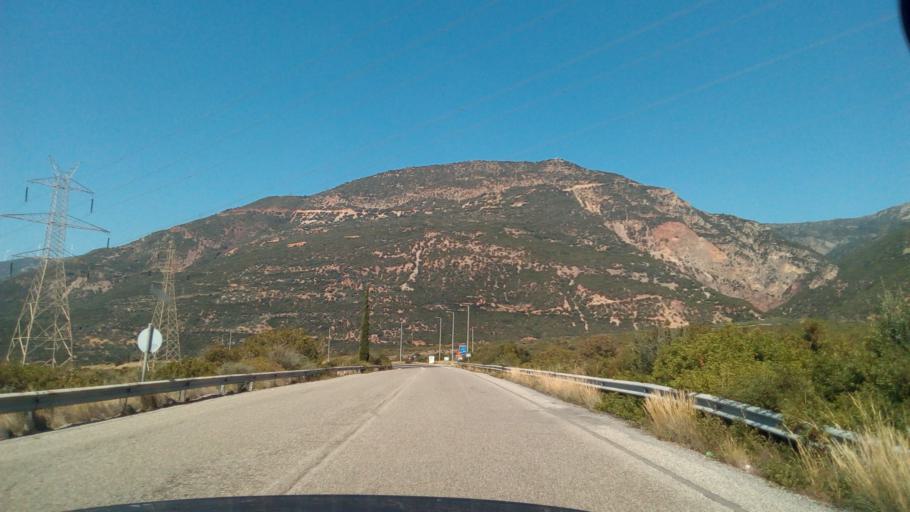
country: GR
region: West Greece
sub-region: Nomos Achaias
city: Selianitika
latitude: 38.3787
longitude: 22.0941
